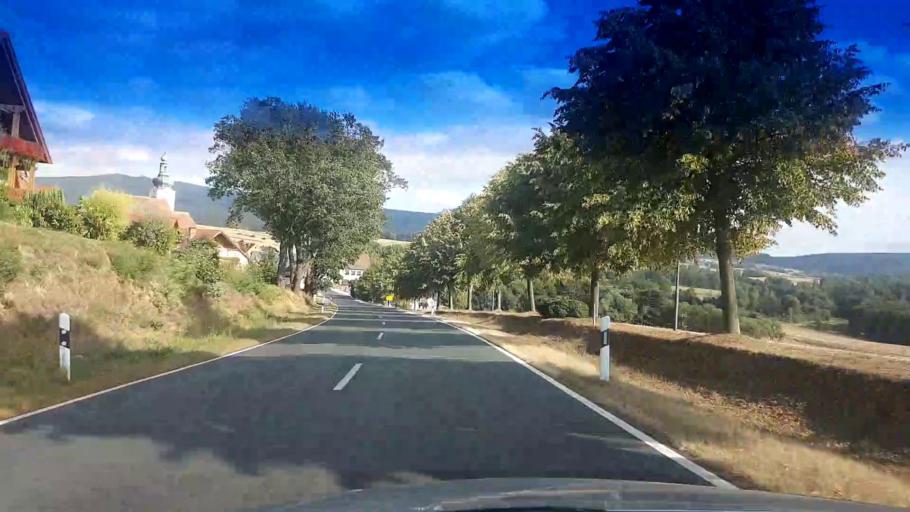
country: DE
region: Bavaria
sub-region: Upper Palatinate
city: Neualbenreuth
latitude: 49.9799
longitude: 12.4367
